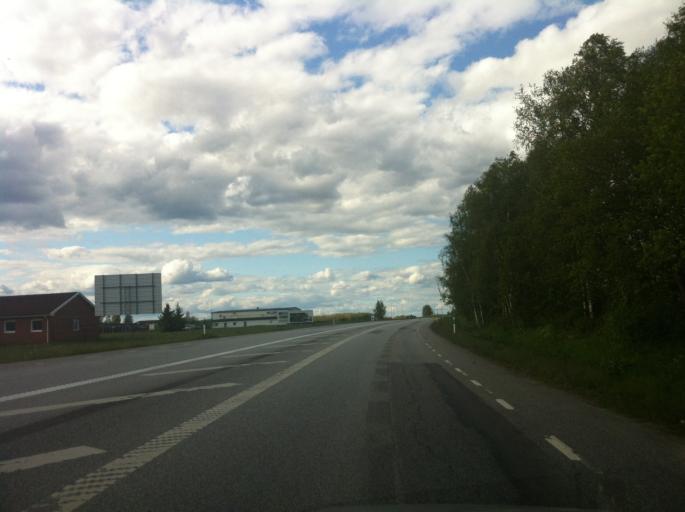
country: SE
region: Vaermland
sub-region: Storfors Kommun
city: Storfors
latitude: 59.5413
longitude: 14.2785
